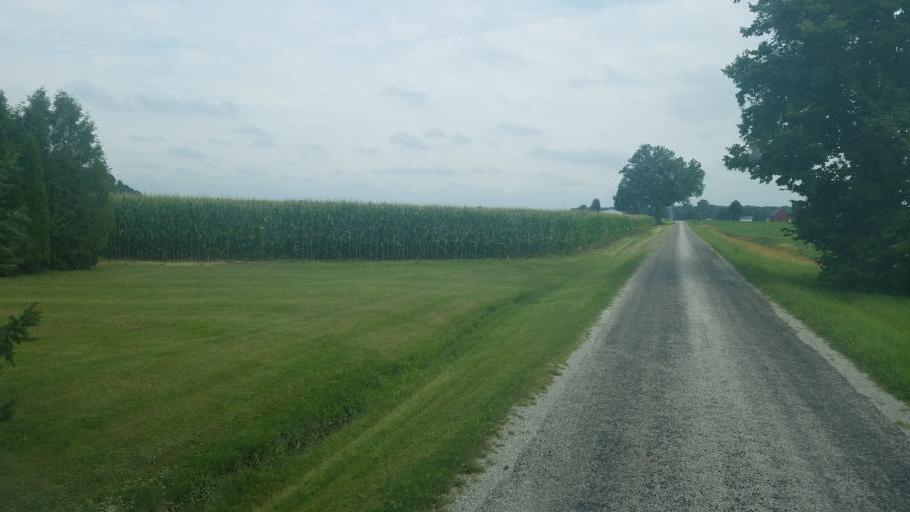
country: US
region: Ohio
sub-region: Morrow County
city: Cardington
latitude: 40.5046
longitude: -82.9817
